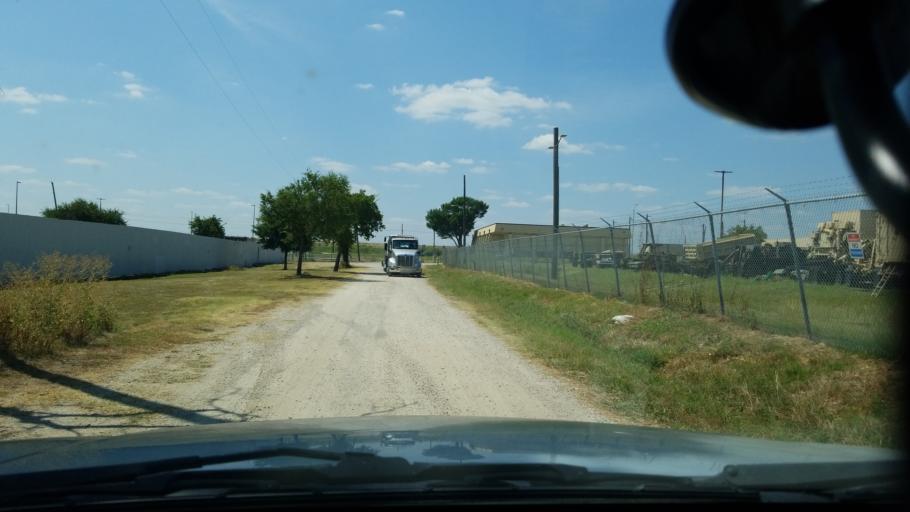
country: US
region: Texas
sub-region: Dallas County
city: Grand Prairie
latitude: 32.7398
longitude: -96.9533
